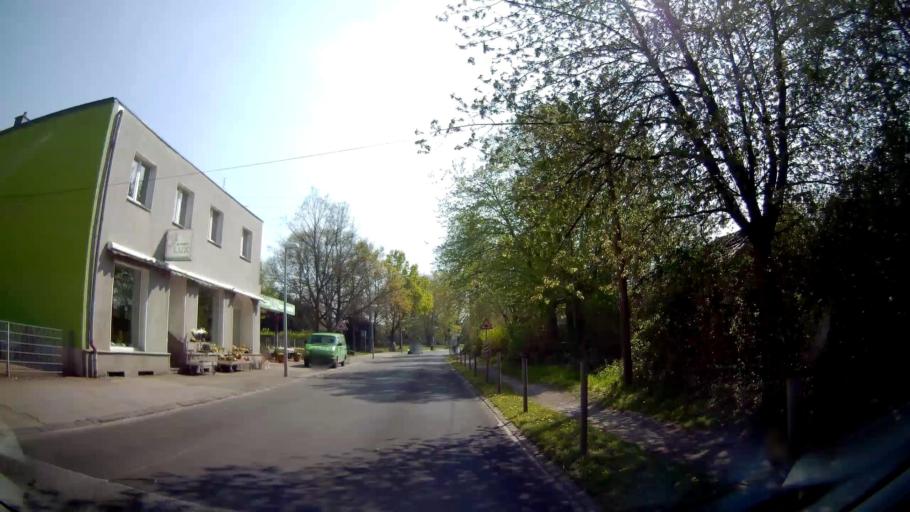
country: DE
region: North Rhine-Westphalia
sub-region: Regierungsbezirk Munster
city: Gelsenkirchen
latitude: 51.5267
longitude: 7.1285
